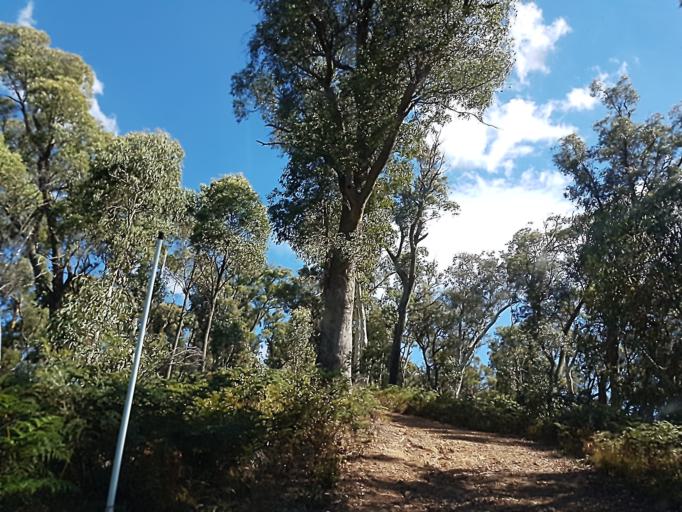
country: AU
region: Victoria
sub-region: Alpine
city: Mount Beauty
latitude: -36.8797
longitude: 147.0257
